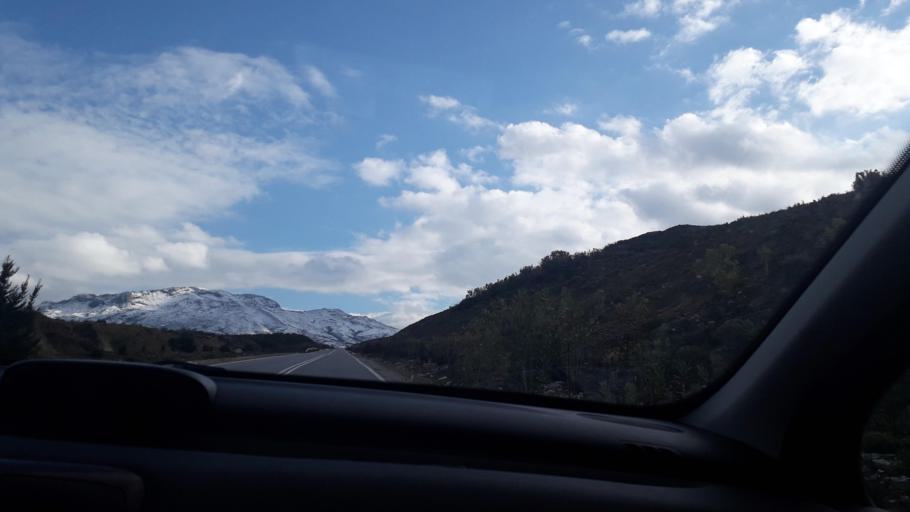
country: GR
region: Crete
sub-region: Nomos Rethymnis
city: Agia Foteini
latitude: 35.2743
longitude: 24.5603
